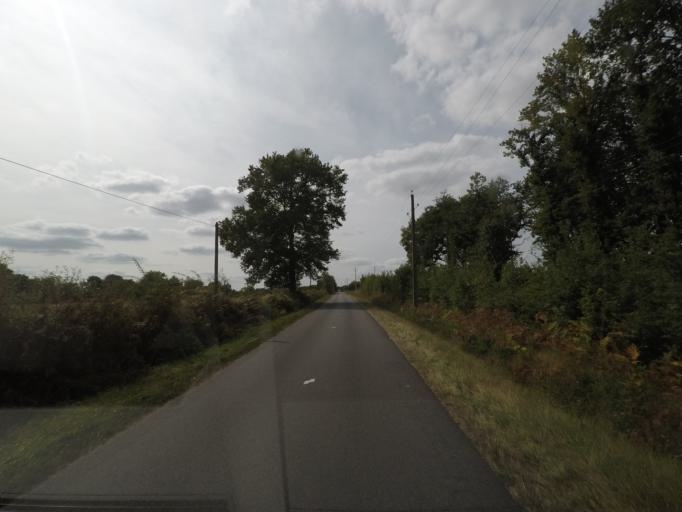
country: FR
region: Poitou-Charentes
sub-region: Departement de la Charente
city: Saint-Claud
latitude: 45.9431
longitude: 0.5130
